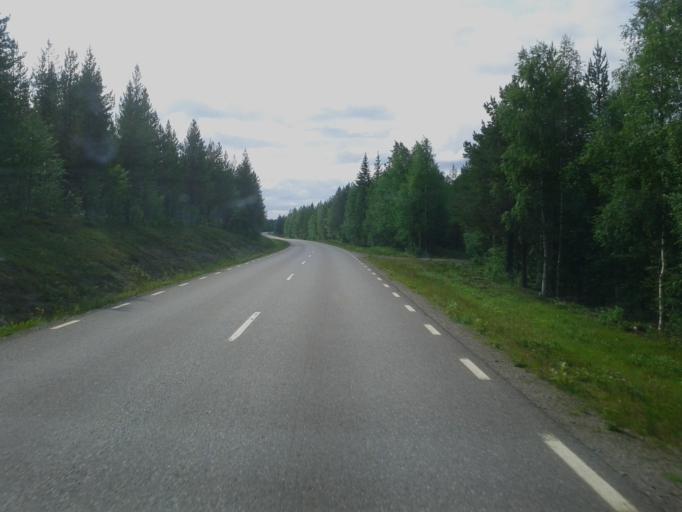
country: SE
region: Vaesterbotten
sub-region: Lycksele Kommun
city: Soderfors
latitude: 65.2561
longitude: 18.2327
